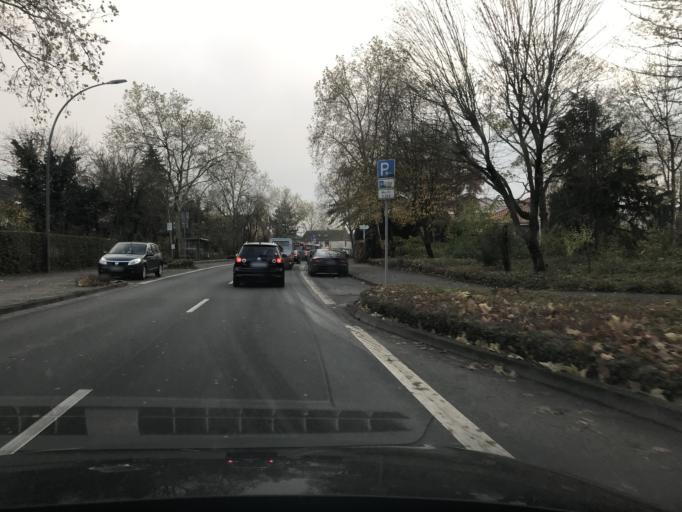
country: DE
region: North Rhine-Westphalia
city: Oelde
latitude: 51.8252
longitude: 8.1459
